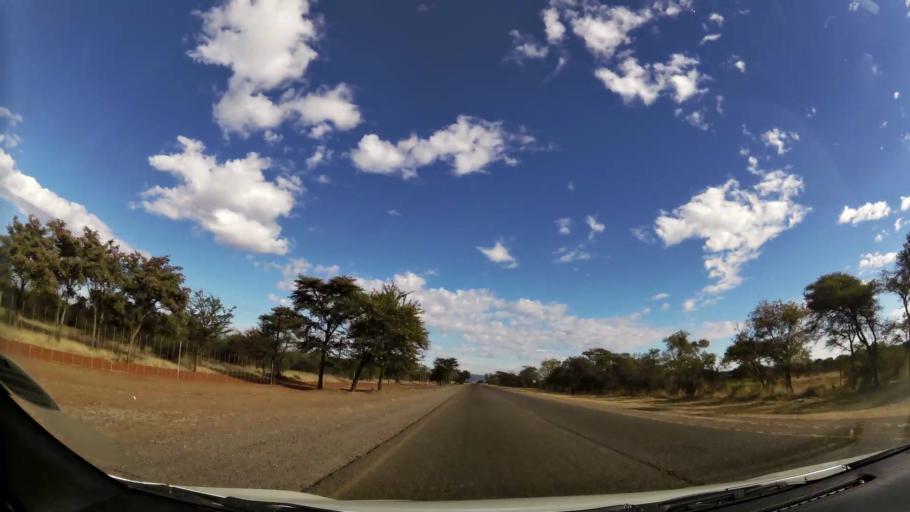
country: ZA
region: Limpopo
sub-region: Waterberg District Municipality
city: Bela-Bela
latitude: -24.9072
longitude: 28.3447
